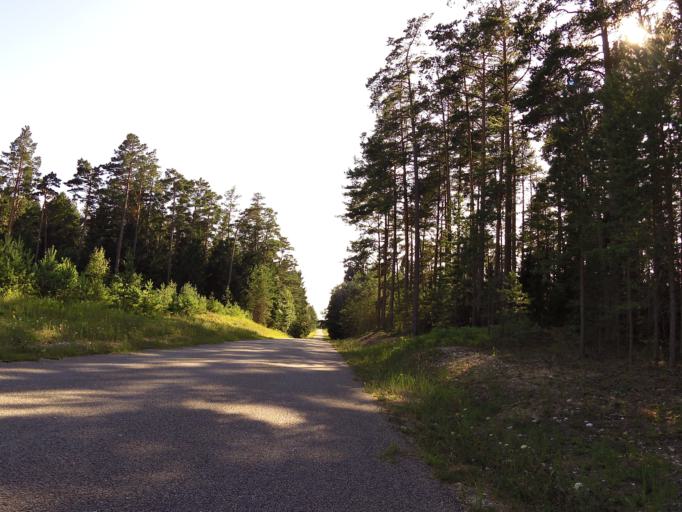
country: EE
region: Hiiumaa
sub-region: Kaerdla linn
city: Kardla
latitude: 58.9074
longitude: 22.2900
